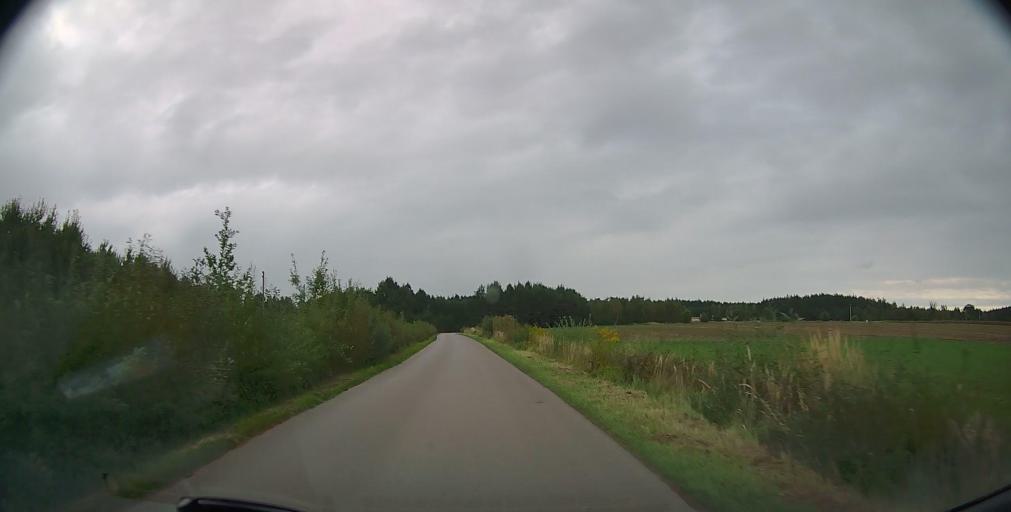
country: PL
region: Masovian Voivodeship
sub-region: Powiat radomski
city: Jedlinsk
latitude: 51.4575
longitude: 21.1037
